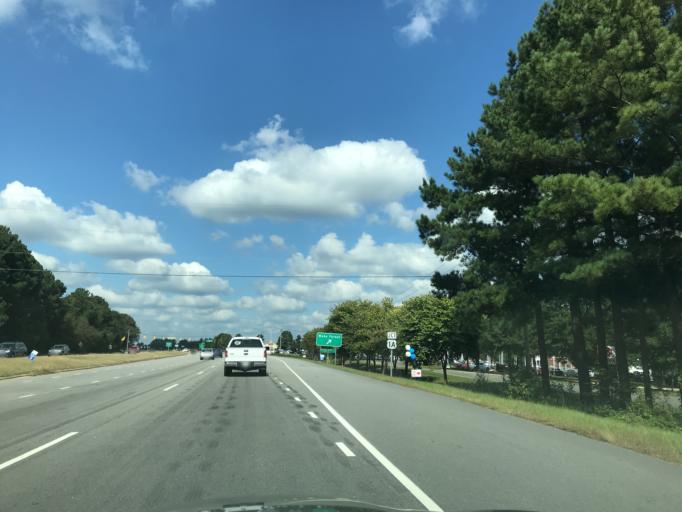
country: US
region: North Carolina
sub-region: Wake County
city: Wake Forest
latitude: 35.9434
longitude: -78.5395
